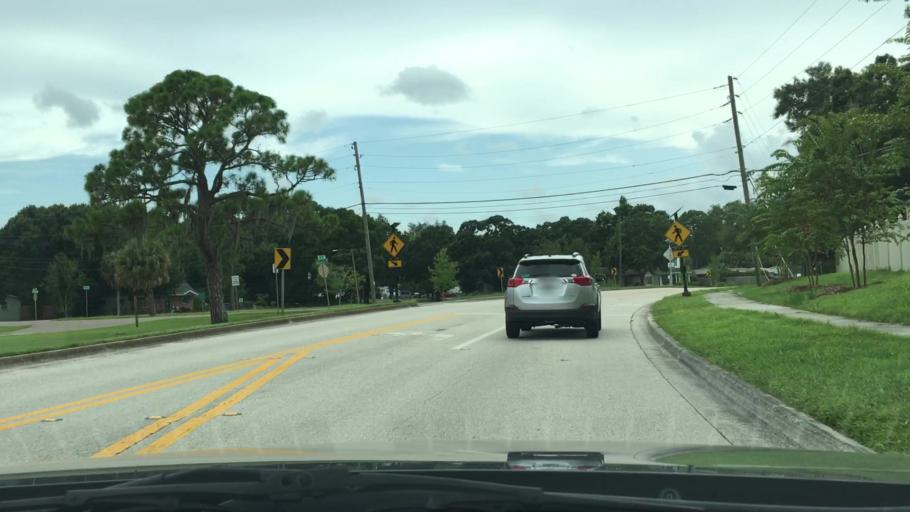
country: US
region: Florida
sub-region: Pinellas County
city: Gandy
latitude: 27.8479
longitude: -82.6297
